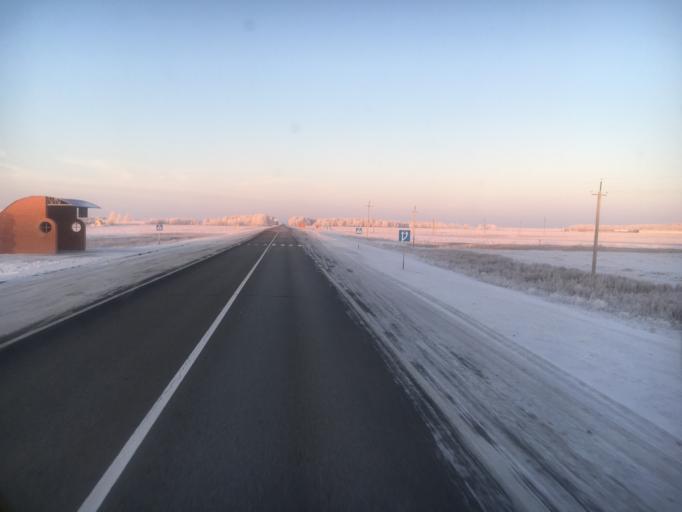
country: KZ
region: Soltustik Qazaqstan
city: Smirnovo
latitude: 54.3438
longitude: 69.1589
